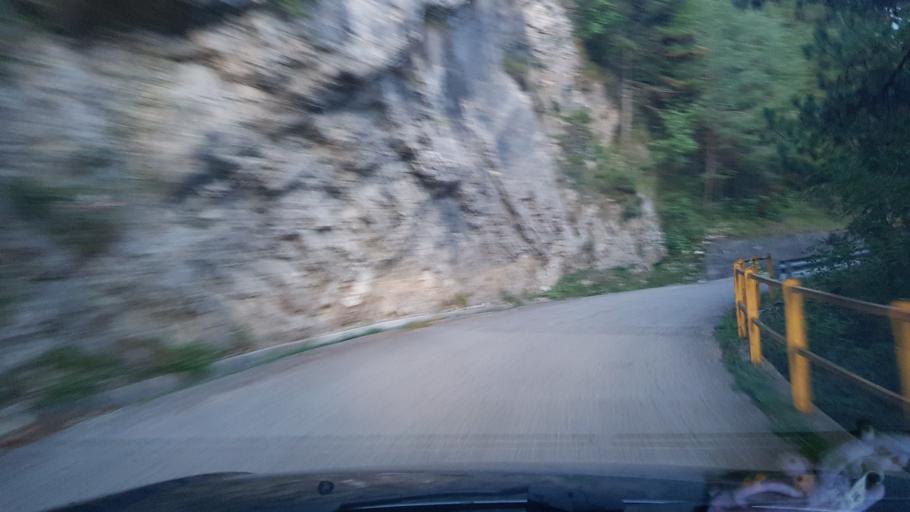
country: IT
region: Friuli Venezia Giulia
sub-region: Provincia di Pordenone
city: Frisanco
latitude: 46.2565
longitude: 12.7282
